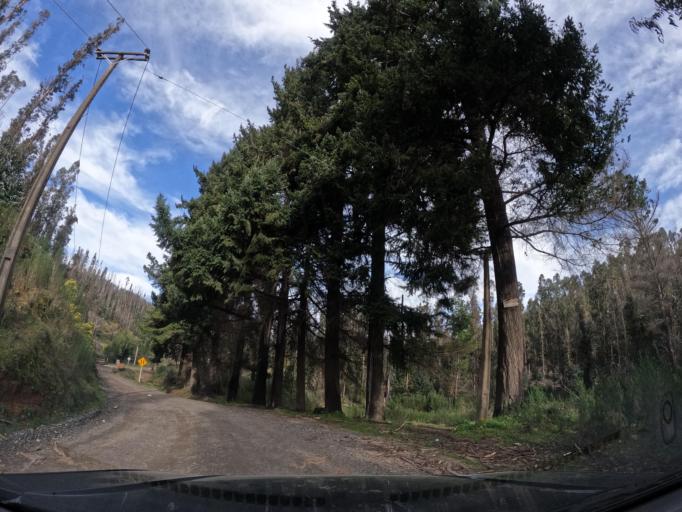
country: CL
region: Biobio
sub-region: Provincia de Concepcion
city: Chiguayante
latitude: -37.0120
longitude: -72.9110
